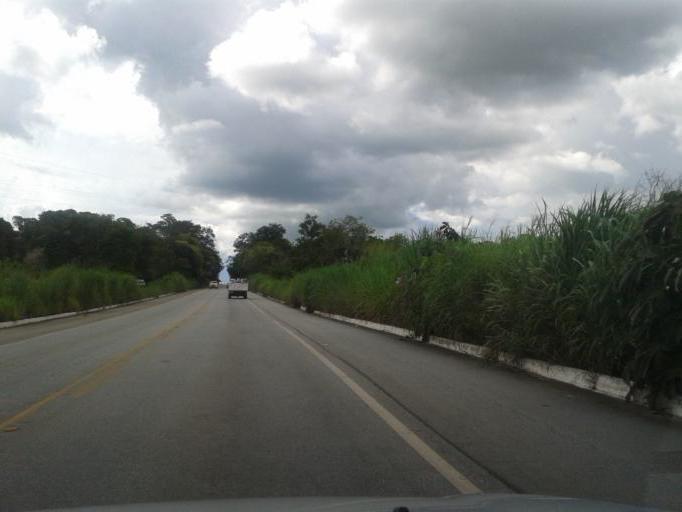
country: BR
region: Goias
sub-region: Goias
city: Goias
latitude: -15.8627
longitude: -50.0891
